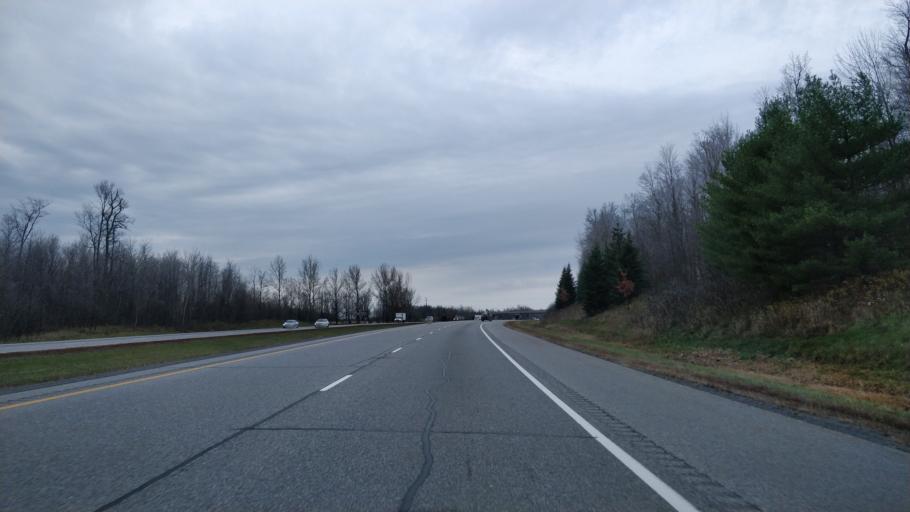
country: CA
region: Ontario
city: Bells Corners
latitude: 45.1314
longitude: -75.6751
